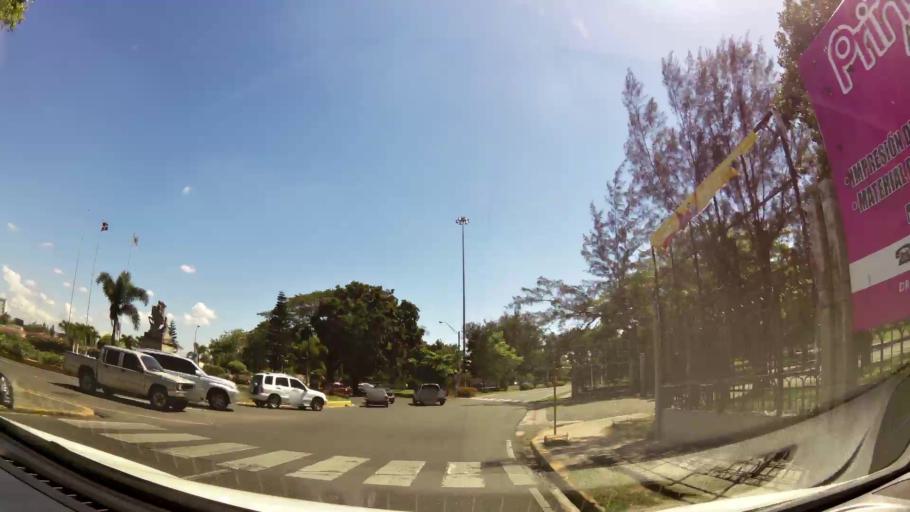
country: DO
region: Santiago
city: Santiago de los Caballeros
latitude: 19.4506
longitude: -70.6909
